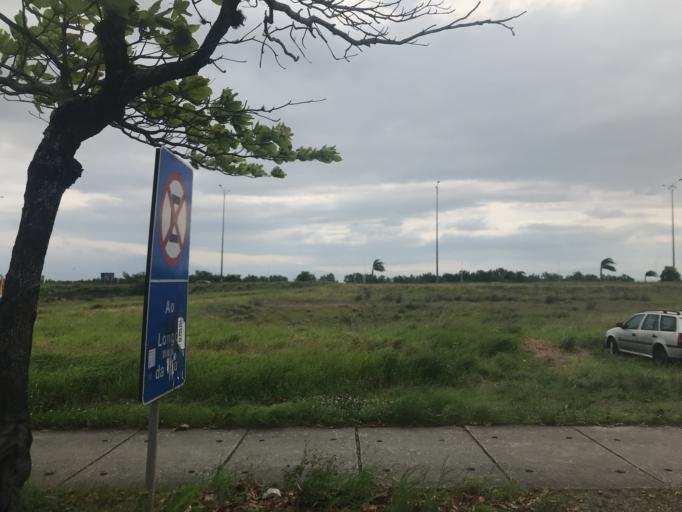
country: BR
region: Santa Catarina
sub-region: Florianopolis
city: Costeira do Pirajubae
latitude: -27.6255
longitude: -48.5256
